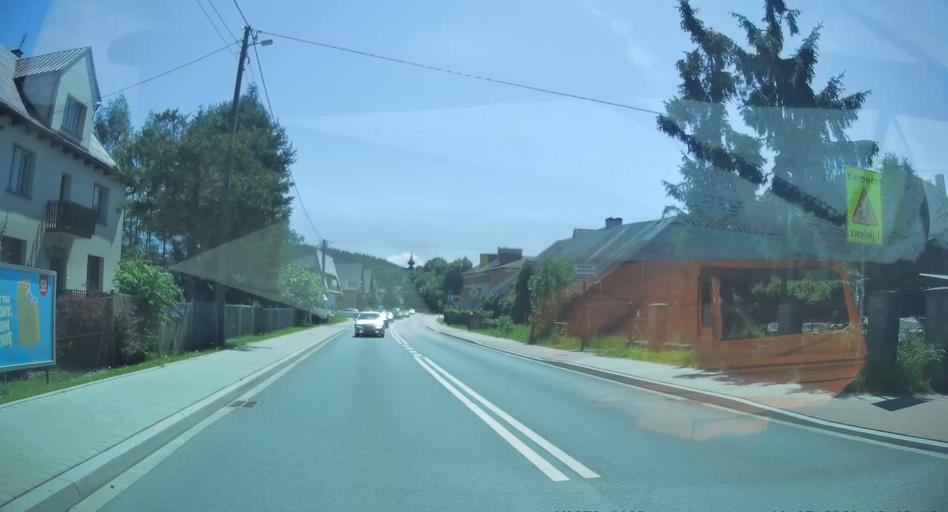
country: PL
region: Lesser Poland Voivodeship
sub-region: Powiat nowosadecki
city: Krynica-Zdroj
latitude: 49.3989
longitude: 20.9564
